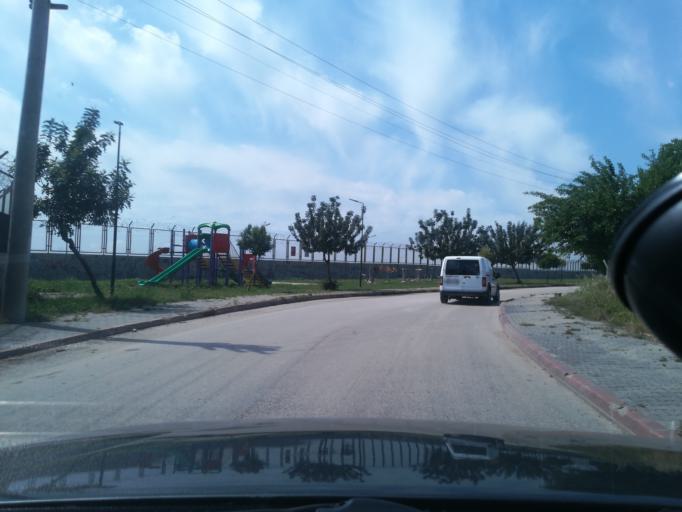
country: TR
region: Adana
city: Seyhan
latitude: 36.9875
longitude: 35.2861
